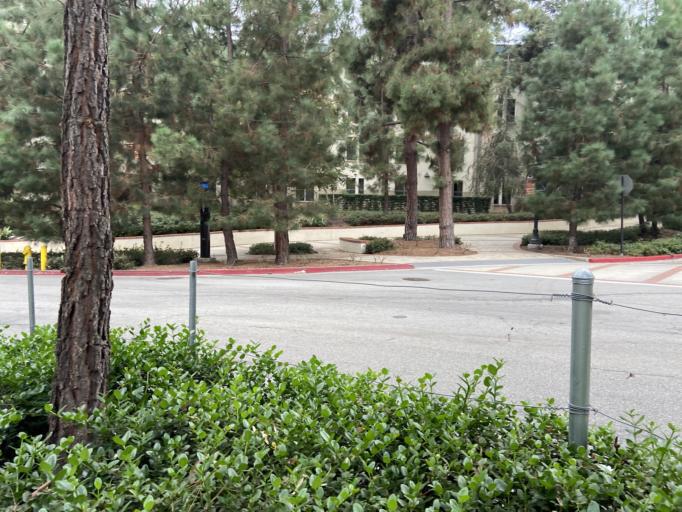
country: US
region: California
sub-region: Los Angeles County
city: Westwood, Los Angeles
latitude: 34.0713
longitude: -118.4495
